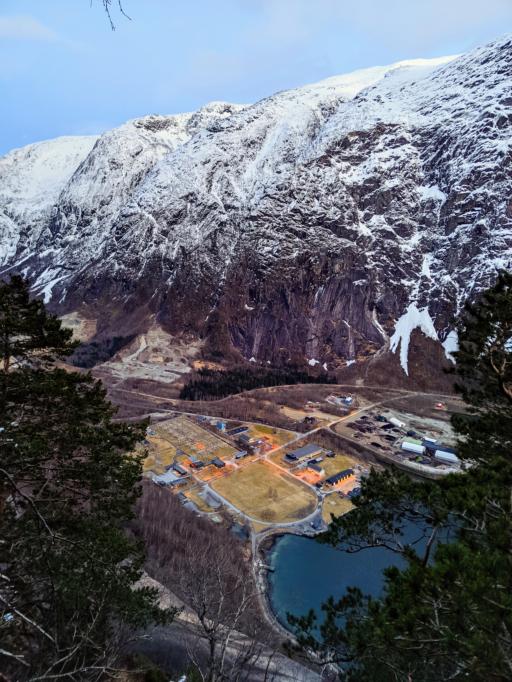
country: NO
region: Hordaland
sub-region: Eidfjord
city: Eidfjord
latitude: 60.5025
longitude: 7.1316
